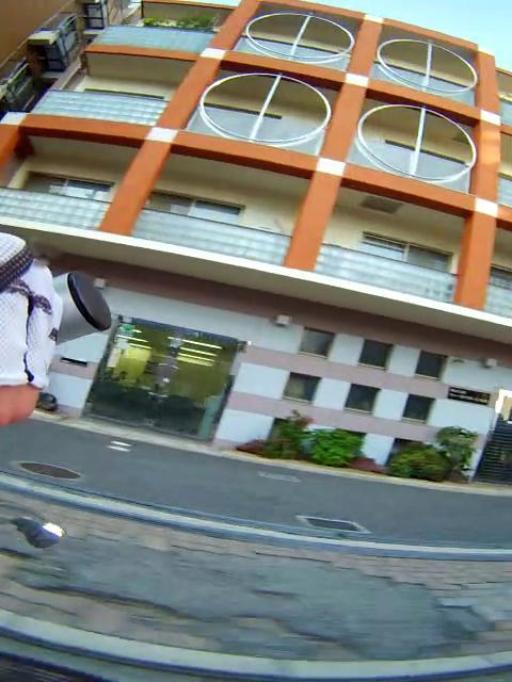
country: JP
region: Hyogo
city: Amagasaki
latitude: 34.7515
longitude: 135.4206
